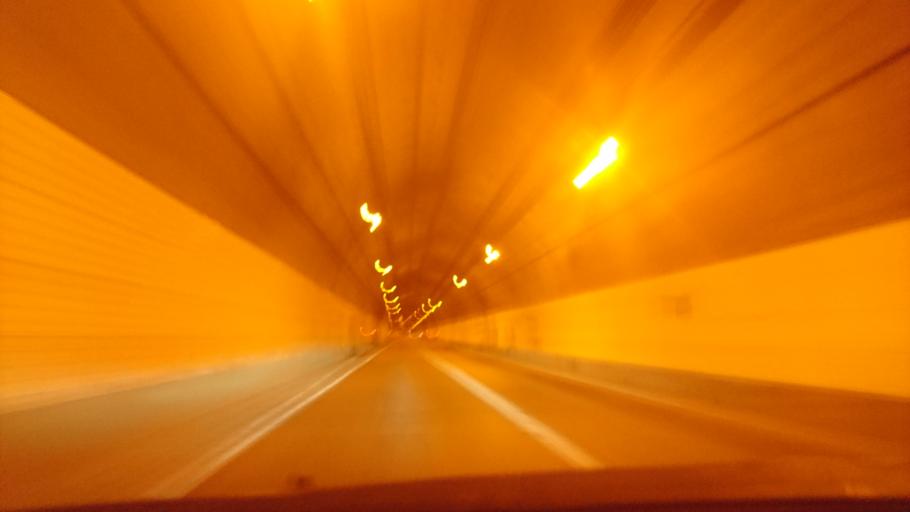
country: JP
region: Iwate
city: Kamaishi
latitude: 39.1832
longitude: 141.8527
